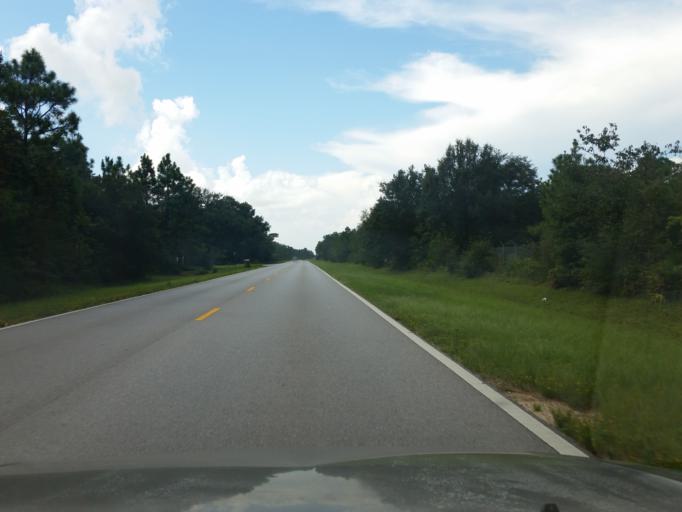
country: US
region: Florida
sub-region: Escambia County
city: Myrtle Grove
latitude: 30.3799
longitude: -87.4023
